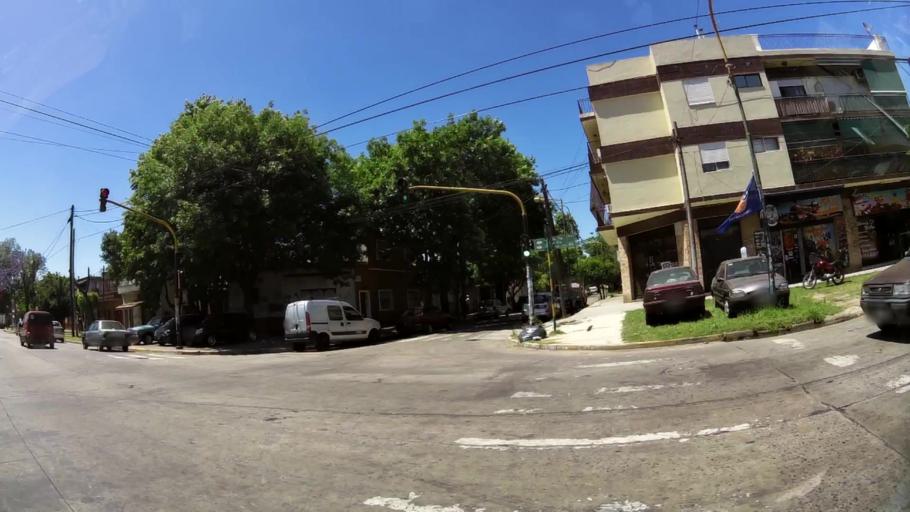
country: AR
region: Buenos Aires
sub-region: Partido de General San Martin
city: General San Martin
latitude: -34.5683
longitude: -58.5173
